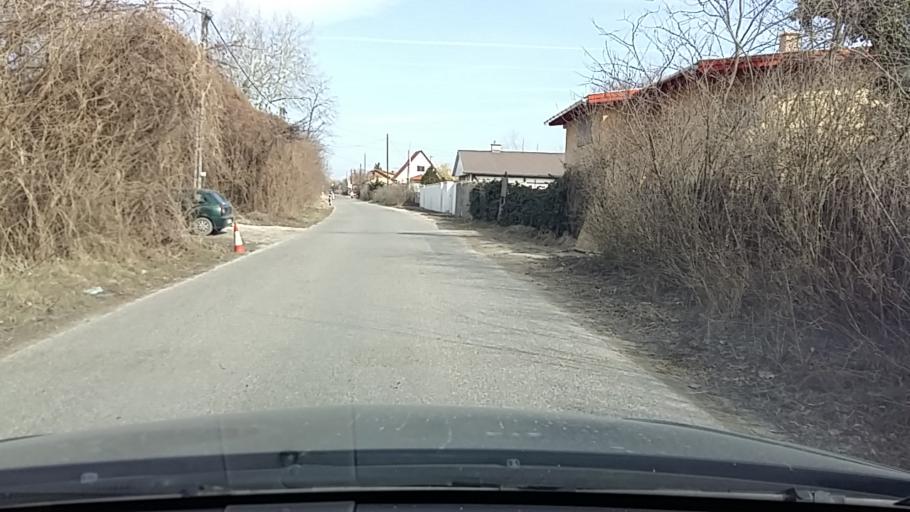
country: HU
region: Pest
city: Dunaharaszti
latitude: 47.3606
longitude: 19.0788
